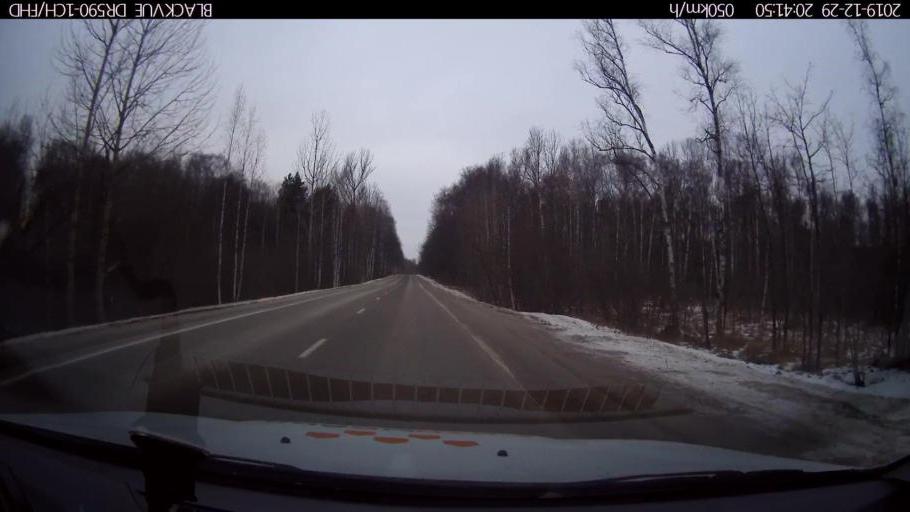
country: RU
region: Nizjnij Novgorod
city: Afonino
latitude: 56.1881
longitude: 44.0348
